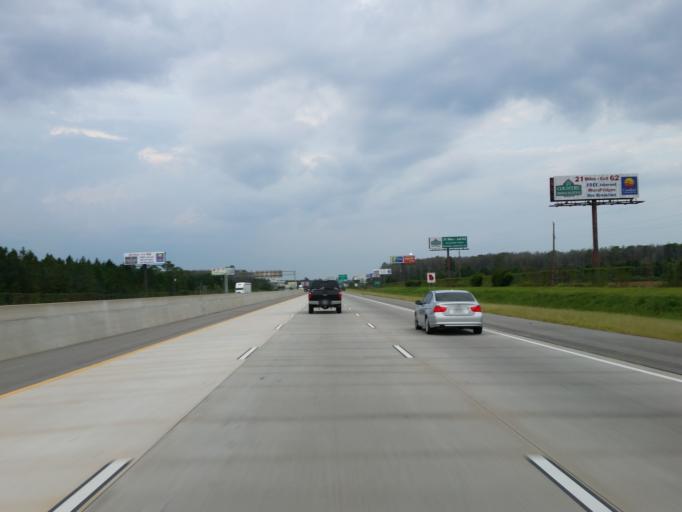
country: US
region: Georgia
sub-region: Cook County
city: Sparks
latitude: 31.1516
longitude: -83.4445
